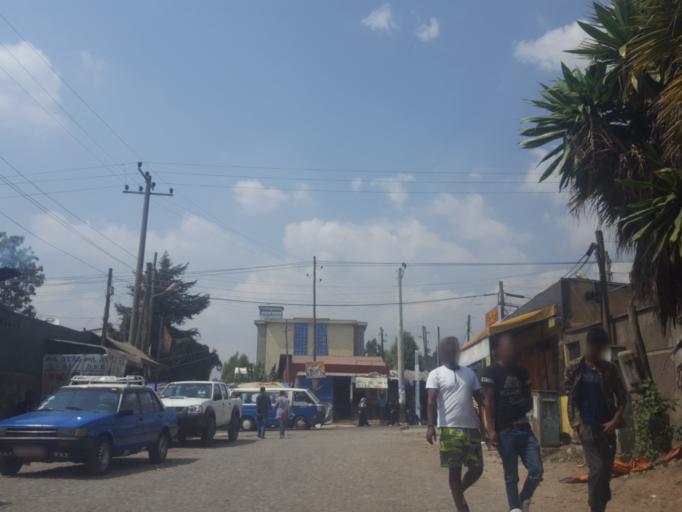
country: ET
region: Adis Abeba
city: Addis Ababa
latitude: 9.0630
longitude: 38.7205
